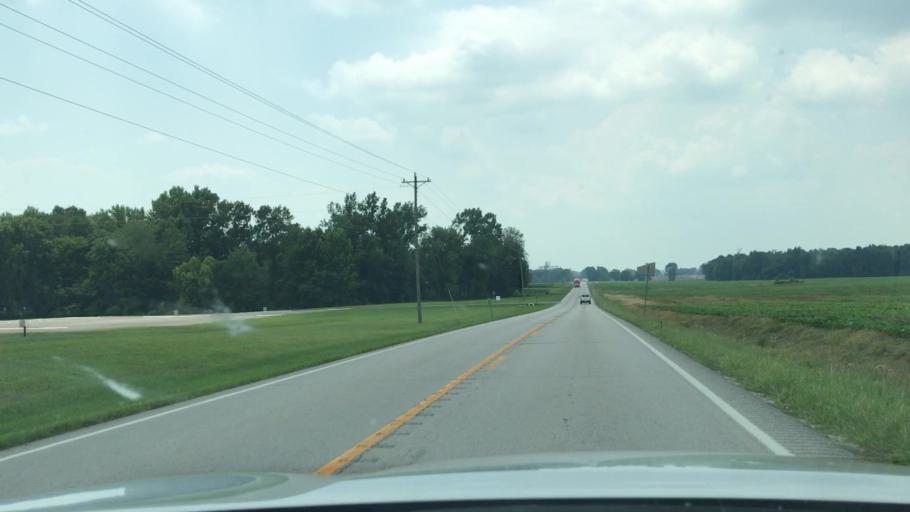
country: US
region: Kentucky
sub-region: Todd County
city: Guthrie
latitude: 36.6695
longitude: -87.1615
